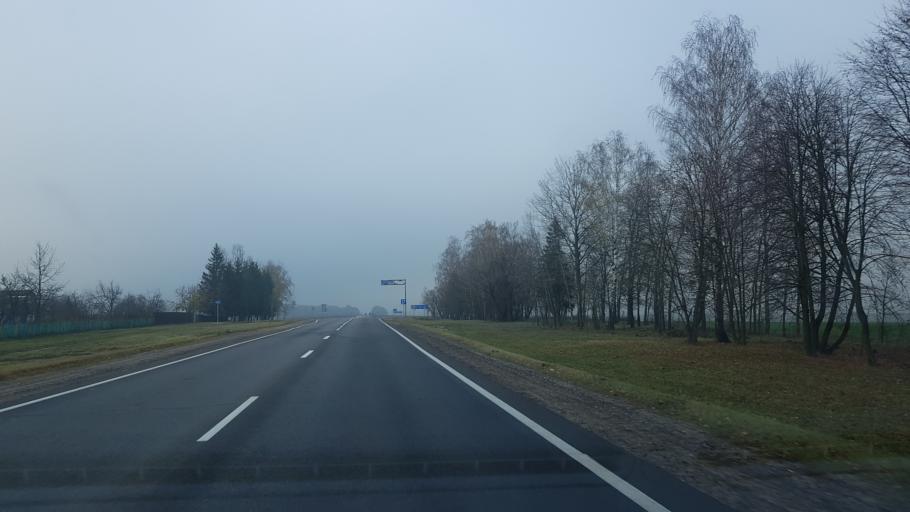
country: BY
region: Mogilev
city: Babruysk
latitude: 53.1798
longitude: 29.3490
